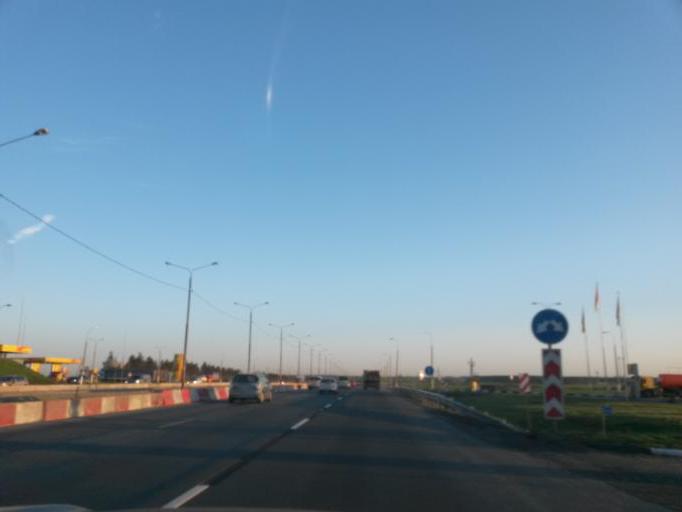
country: RU
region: Moskovskaya
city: Klimovsk
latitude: 55.3591
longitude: 37.5979
